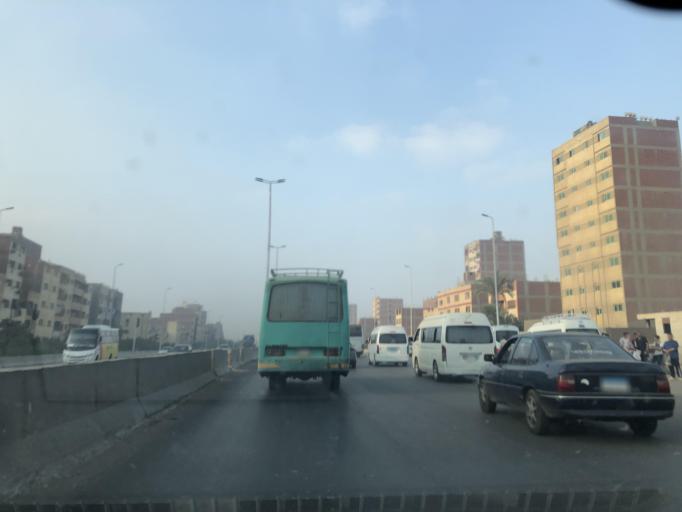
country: EG
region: Al Jizah
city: Awsim
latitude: 30.0721
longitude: 31.1757
